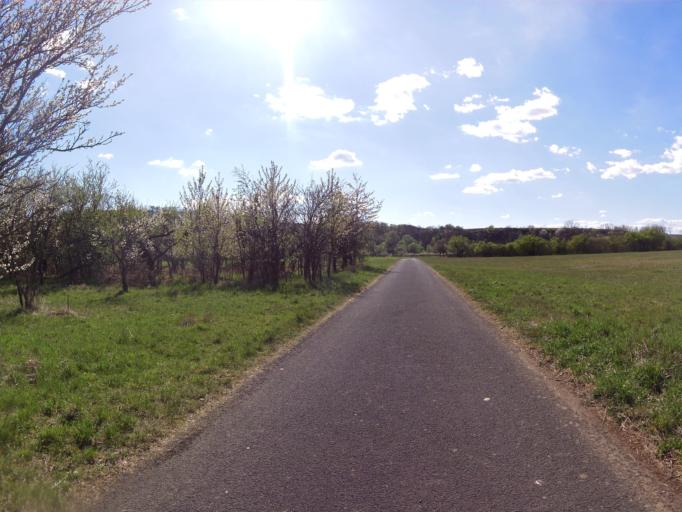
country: DE
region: Bavaria
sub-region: Regierungsbezirk Unterfranken
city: Volkach
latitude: 49.8564
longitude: 10.2131
